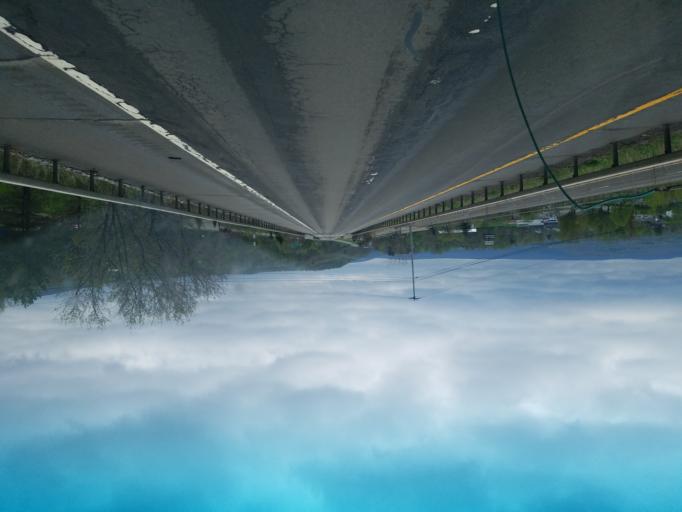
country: US
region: New York
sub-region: Cattaraugus County
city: Randolph
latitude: 42.1596
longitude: -78.9966
